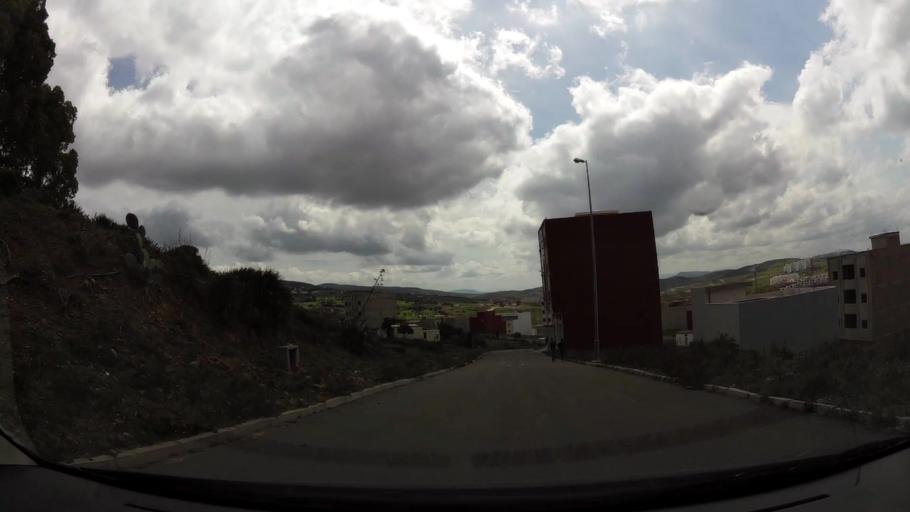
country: MA
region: Tanger-Tetouan
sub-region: Tanger-Assilah
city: Tangier
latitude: 35.7707
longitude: -5.7540
